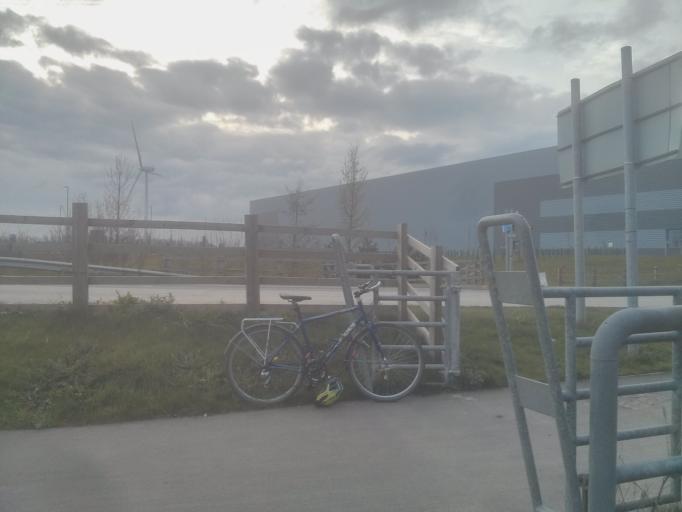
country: GB
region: England
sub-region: City and Borough of Leeds
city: Lofthouse
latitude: 53.7808
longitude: -1.4808
